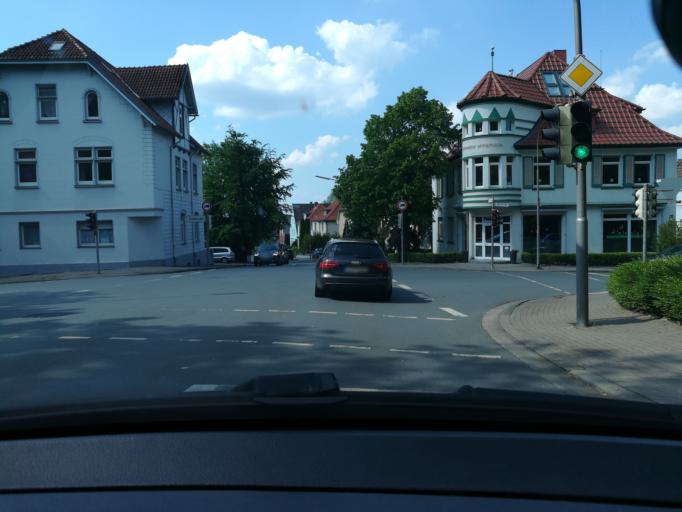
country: DE
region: North Rhine-Westphalia
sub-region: Regierungsbezirk Detmold
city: Herford
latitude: 52.1171
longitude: 8.6856
